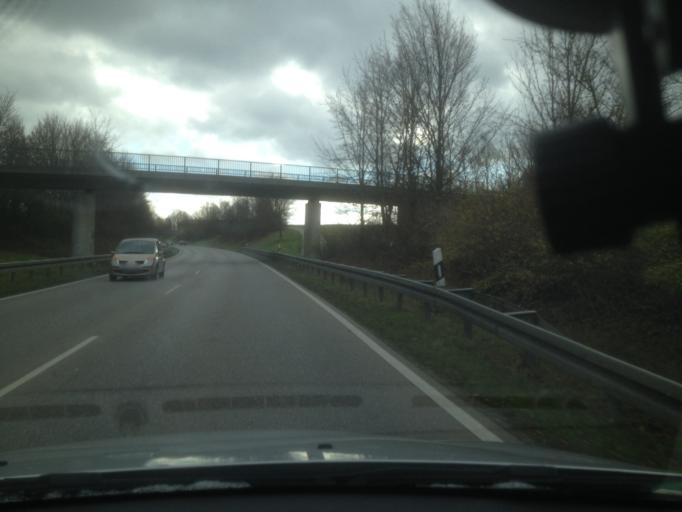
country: DE
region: Bavaria
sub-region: Swabia
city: Mering
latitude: 48.2608
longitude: 10.9706
